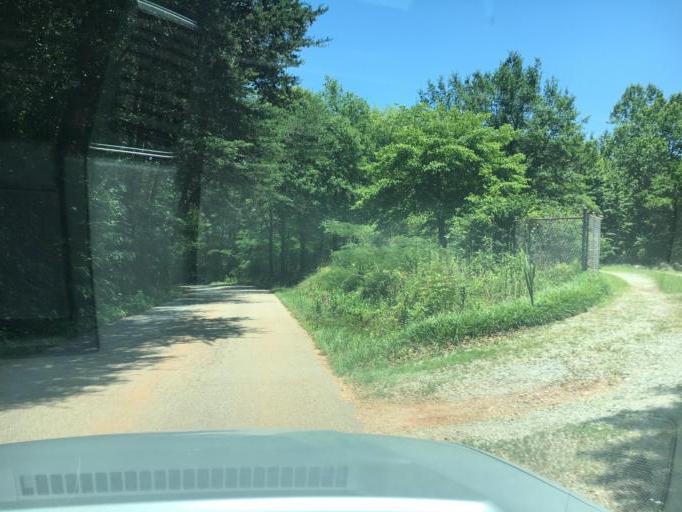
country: US
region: South Carolina
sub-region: Greenville County
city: Greer
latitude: 34.9605
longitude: -82.2178
